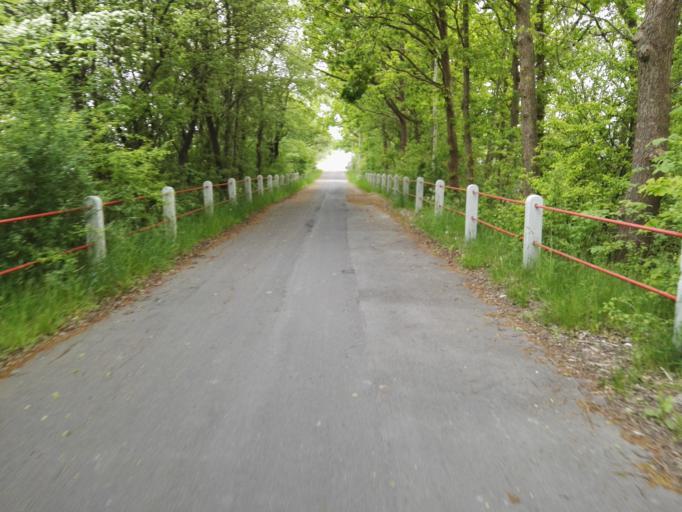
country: DK
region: Capital Region
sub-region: Ballerup Kommune
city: Ballerup
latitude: 55.7258
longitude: 12.3748
